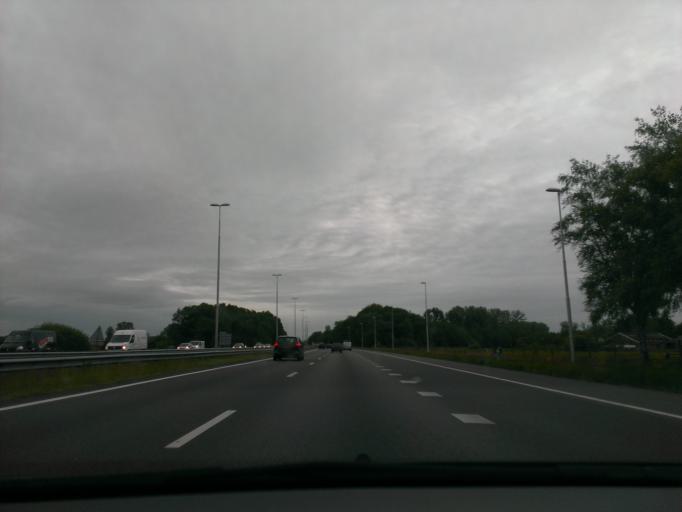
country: NL
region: Gelderland
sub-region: Gemeente Epe
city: Epe
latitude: 52.3289
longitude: 6.0073
